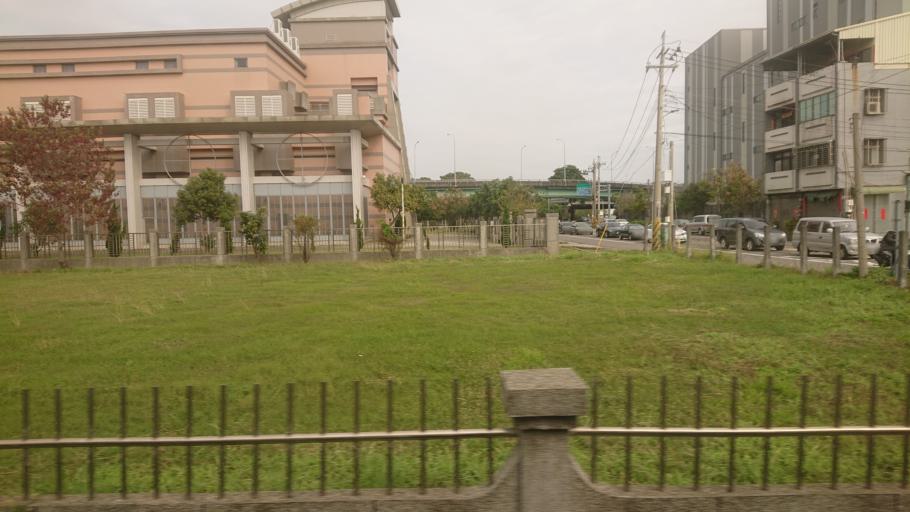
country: TW
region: Taiwan
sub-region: Changhua
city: Chang-hua
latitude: 24.1104
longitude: 120.6070
